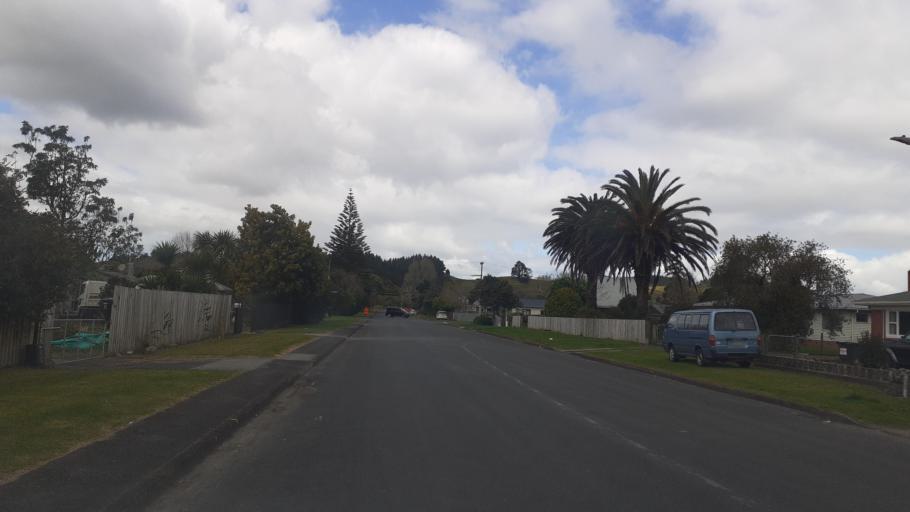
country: NZ
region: Northland
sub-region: Far North District
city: Moerewa
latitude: -35.3883
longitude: 174.0154
